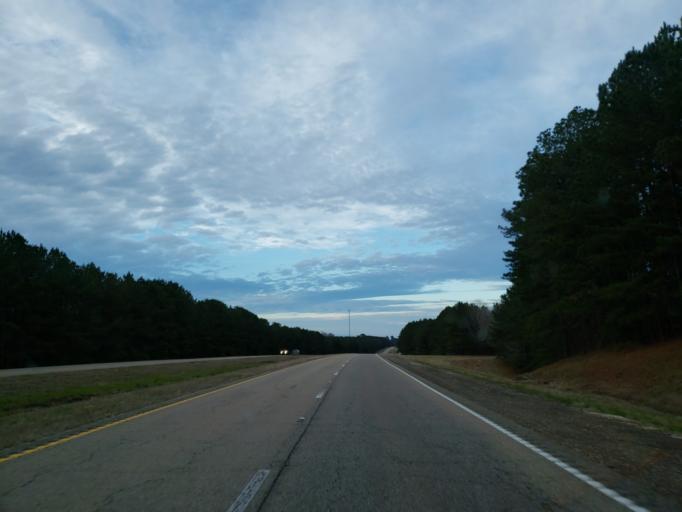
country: US
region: Mississippi
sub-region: Lauderdale County
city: Meridian Station
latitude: 32.6117
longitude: -88.4988
